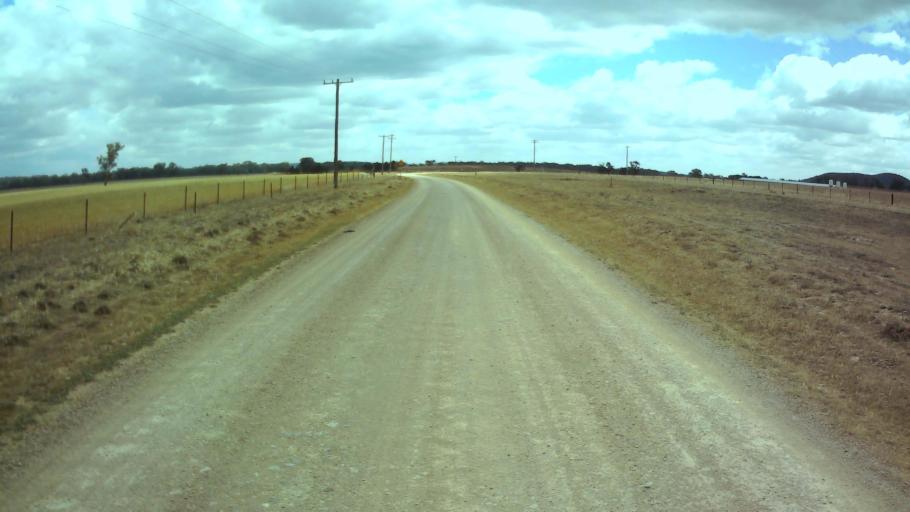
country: AU
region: New South Wales
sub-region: Weddin
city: Grenfell
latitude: -33.9390
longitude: 148.2876
